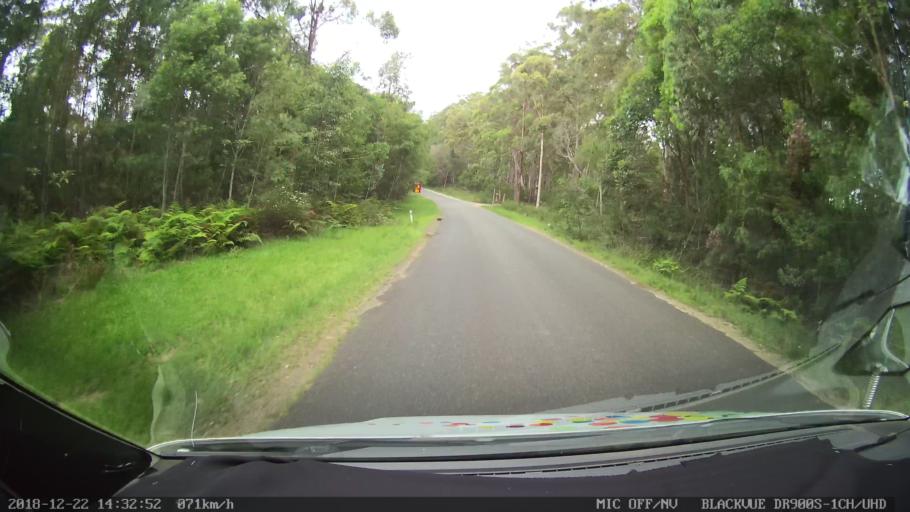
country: AU
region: New South Wales
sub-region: Bellingen
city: Dorrigo
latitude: -30.1078
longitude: 152.6240
